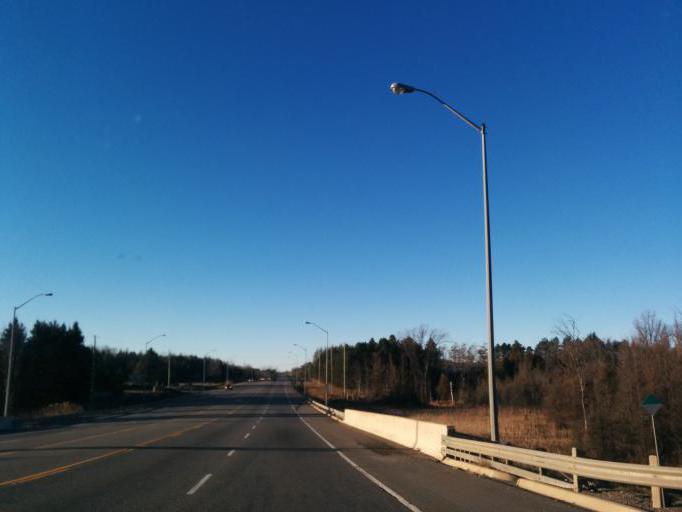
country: CA
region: Ontario
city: Orangeville
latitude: 43.9015
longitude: -80.0520
